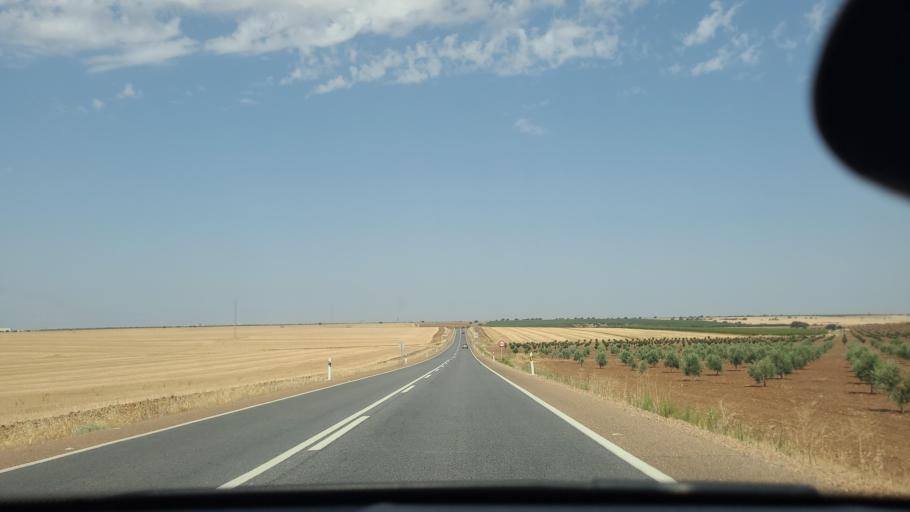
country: ES
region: Extremadura
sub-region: Provincia de Badajoz
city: Entrin Bajo
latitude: 38.6452
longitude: -6.7026
